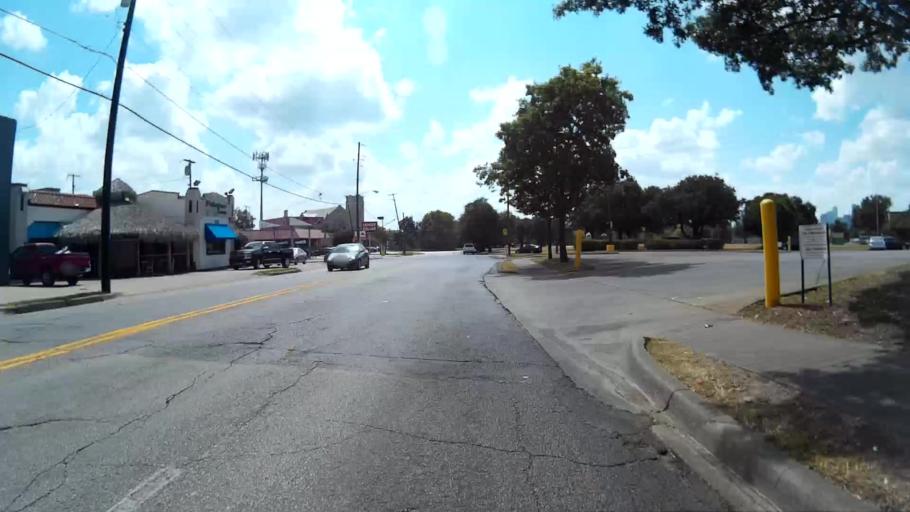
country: US
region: Texas
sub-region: Dallas County
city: Highland Park
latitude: 32.8085
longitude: -96.7702
